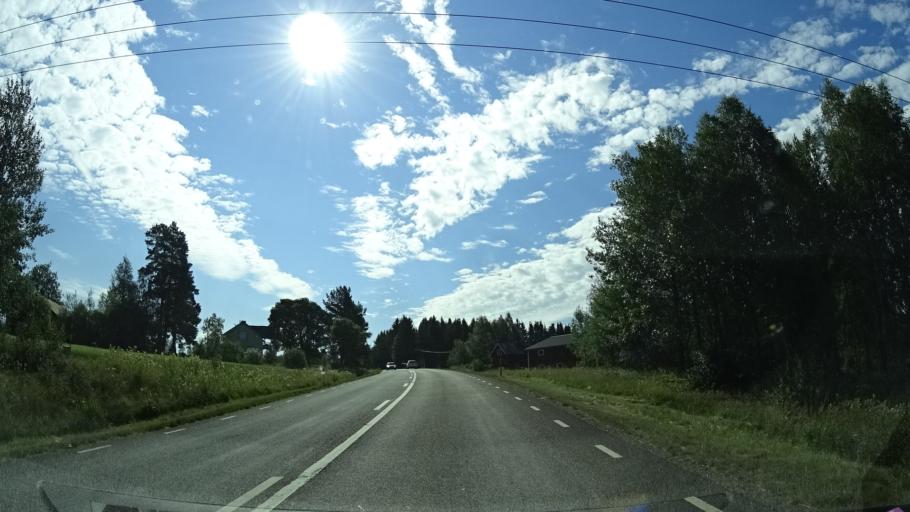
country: SE
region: Vaermland
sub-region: Arjangs Kommun
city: Arjaeng
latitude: 59.4641
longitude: 12.0099
